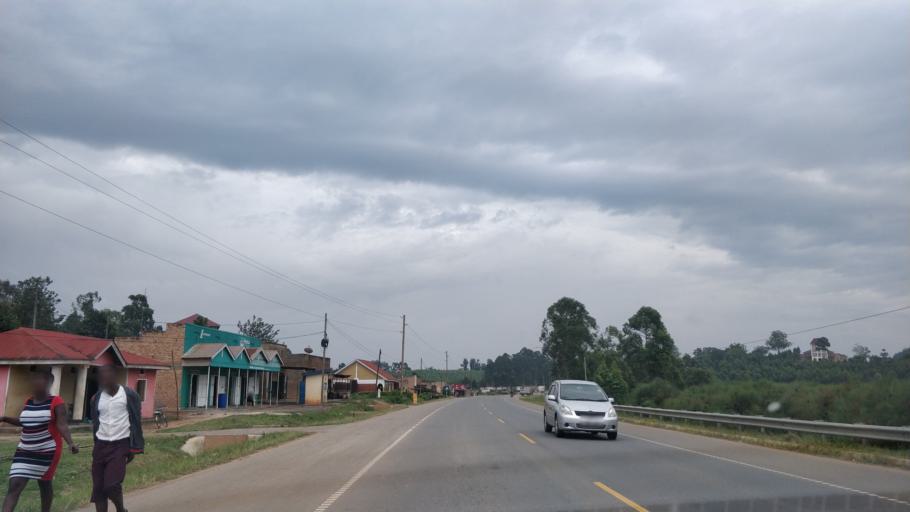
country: UG
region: Western Region
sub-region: Sheema District
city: Kibingo
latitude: -0.6602
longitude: 30.4569
